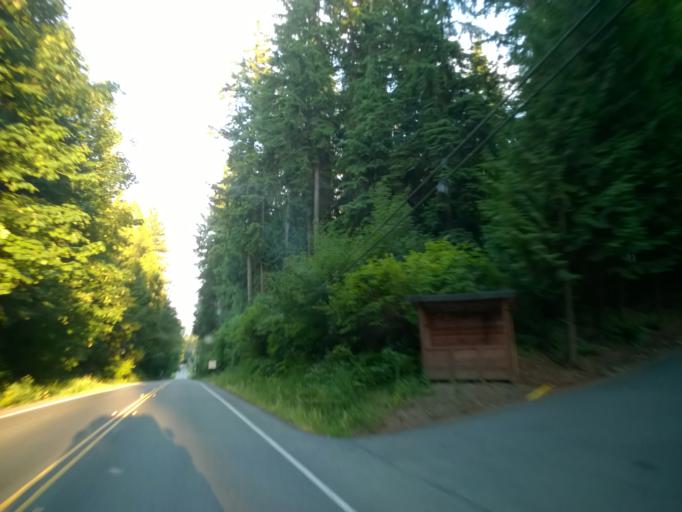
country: US
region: Washington
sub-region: King County
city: Cottage Lake
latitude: 47.7590
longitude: -122.0314
